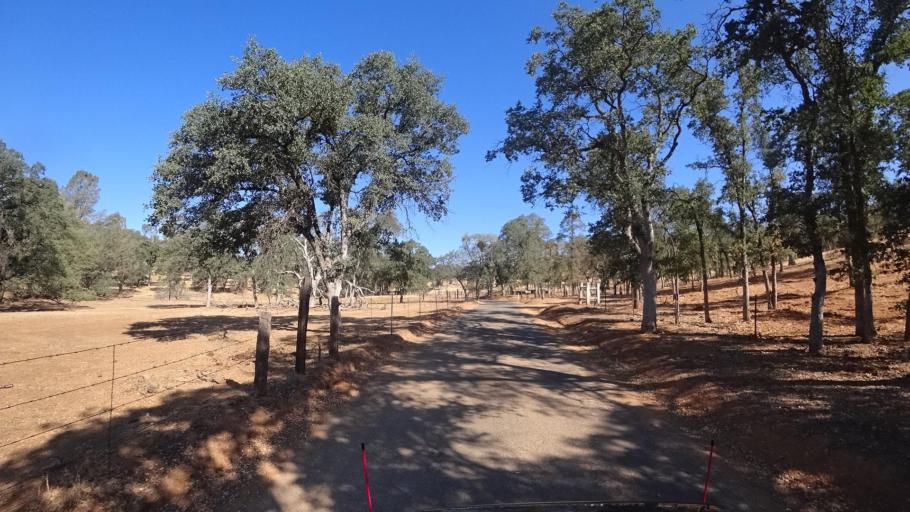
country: US
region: California
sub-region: Mariposa County
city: Mariposa
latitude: 37.6045
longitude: -120.2004
